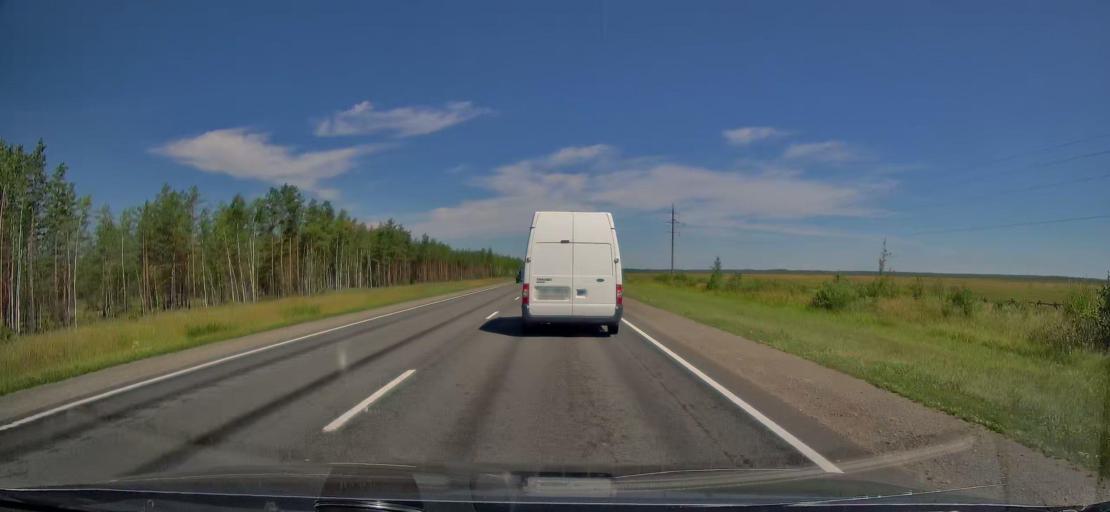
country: RU
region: Vologda
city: Khokhlovo
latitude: 58.9809
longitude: 37.3275
